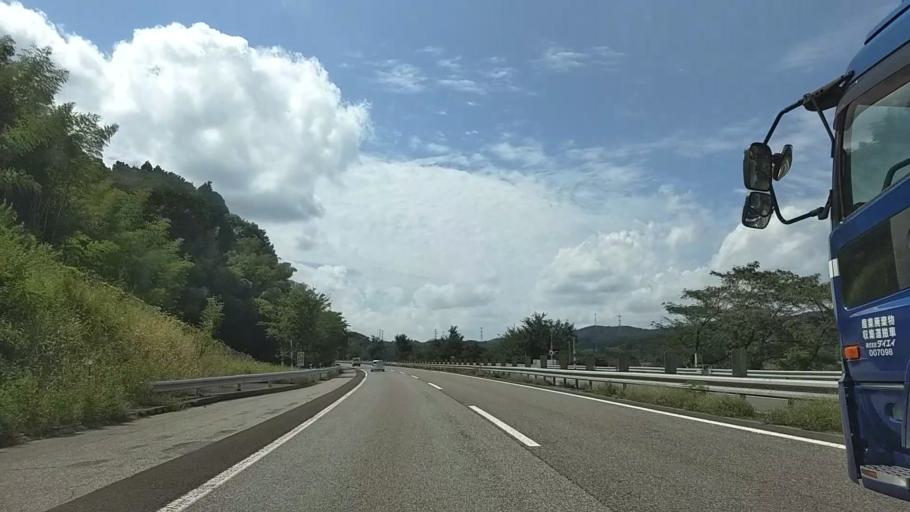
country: JP
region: Toyama
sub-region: Oyabe Shi
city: Oyabe
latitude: 36.6223
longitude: 136.8281
